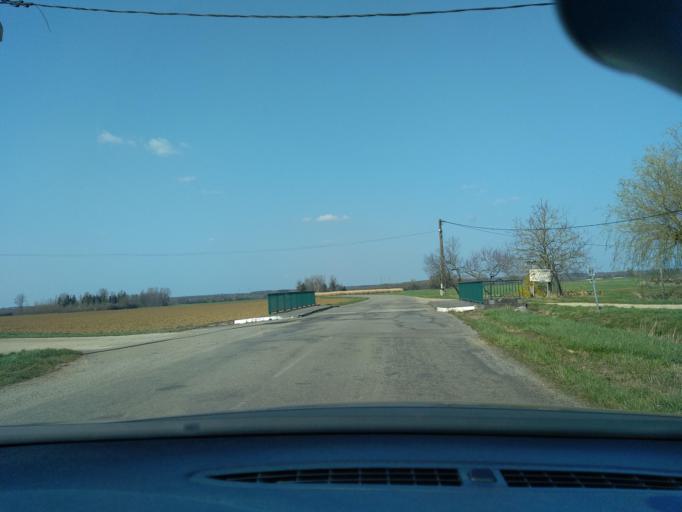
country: FR
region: Franche-Comte
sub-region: Departement du Jura
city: Mont-sous-Vaudrey
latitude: 46.9898
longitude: 5.6057
